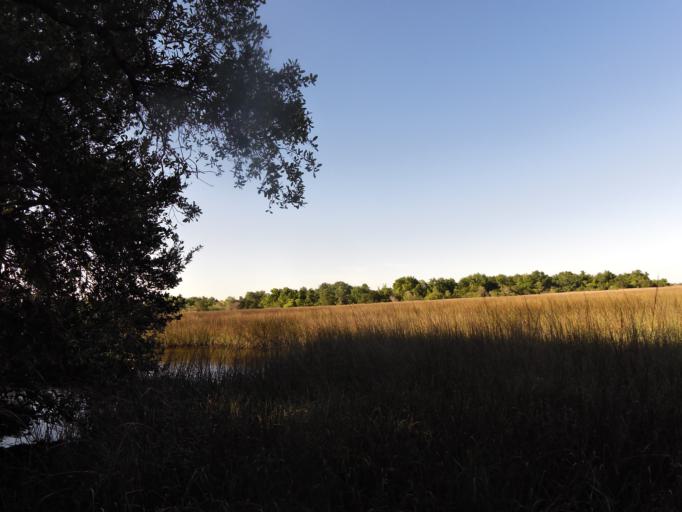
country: US
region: Florida
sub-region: Duval County
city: Atlantic Beach
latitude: 30.3810
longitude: -81.4819
